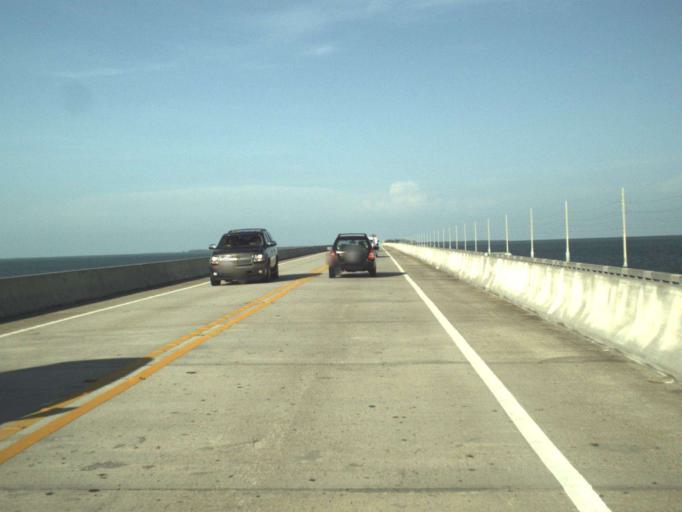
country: US
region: Florida
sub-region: Monroe County
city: Marathon
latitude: 24.7925
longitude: -80.8805
